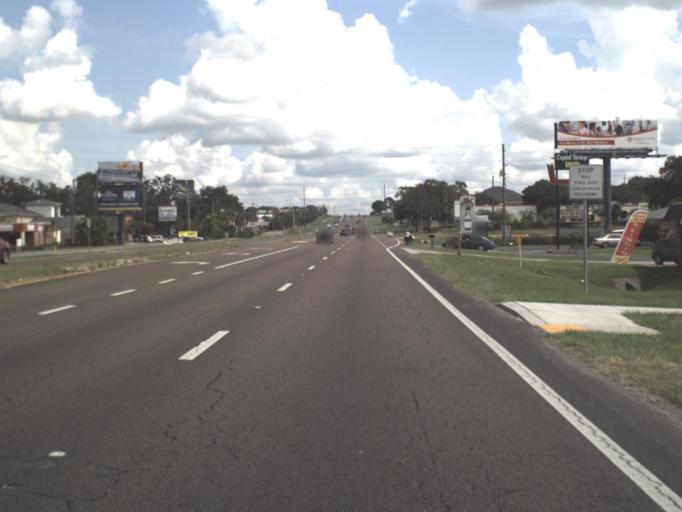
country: US
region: Florida
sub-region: Pasco County
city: Zephyrhills
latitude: 28.2549
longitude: -82.1881
